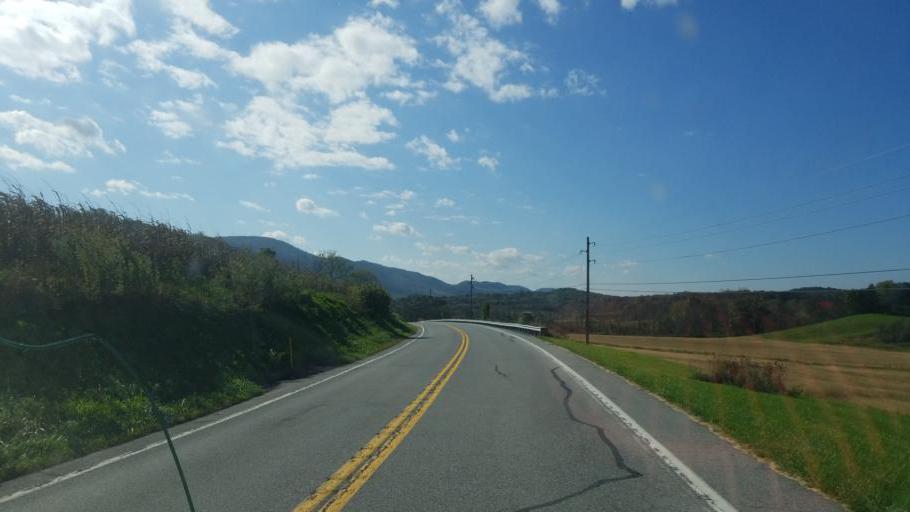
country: US
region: Pennsylvania
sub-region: Bedford County
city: Bedford
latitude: 40.0639
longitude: -78.5509
